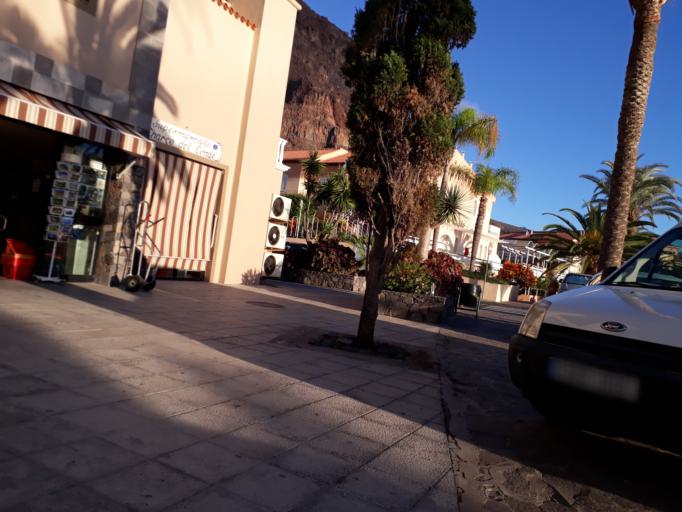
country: ES
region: Canary Islands
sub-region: Provincia de Santa Cruz de Tenerife
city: Alajero
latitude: 28.0859
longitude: -17.3371
